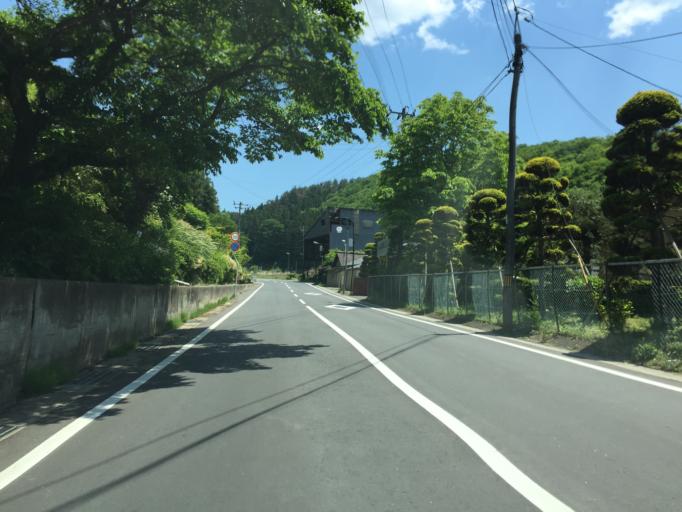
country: JP
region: Fukushima
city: Funehikimachi-funehiki
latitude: 37.5126
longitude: 140.6628
